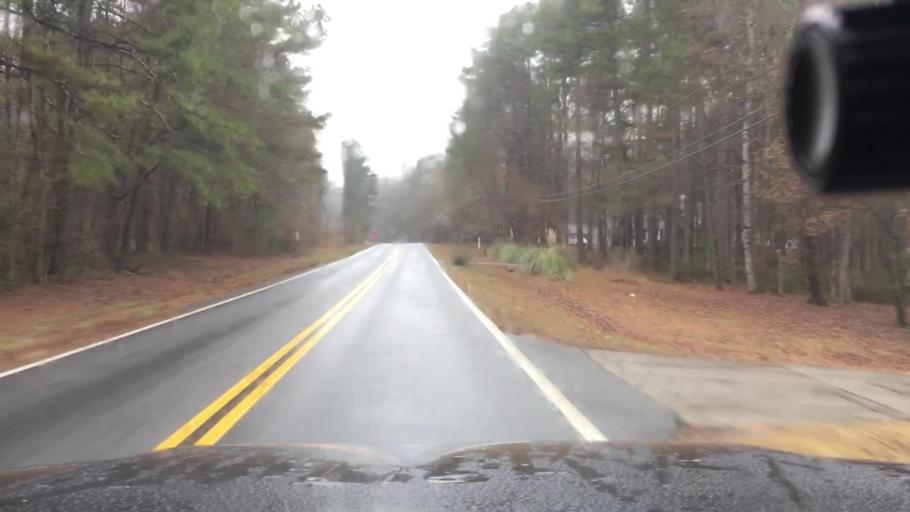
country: US
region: Georgia
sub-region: Coweta County
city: East Newnan
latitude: 33.4169
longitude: -84.7026
